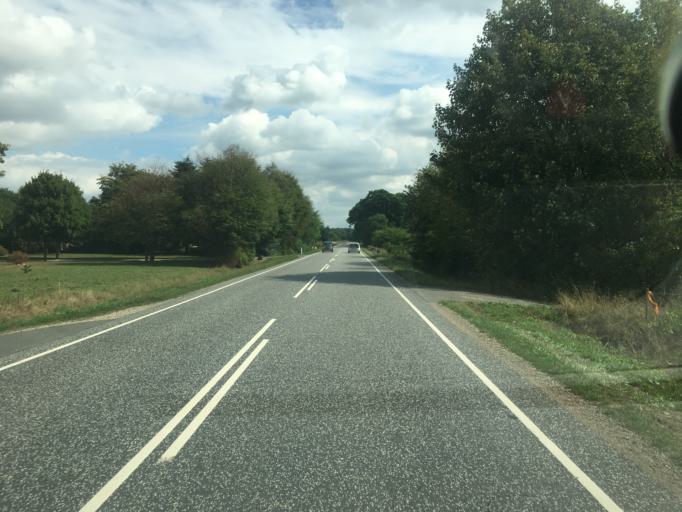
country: DK
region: South Denmark
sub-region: Aabenraa Kommune
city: Aabenraa
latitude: 54.9819
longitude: 9.3550
